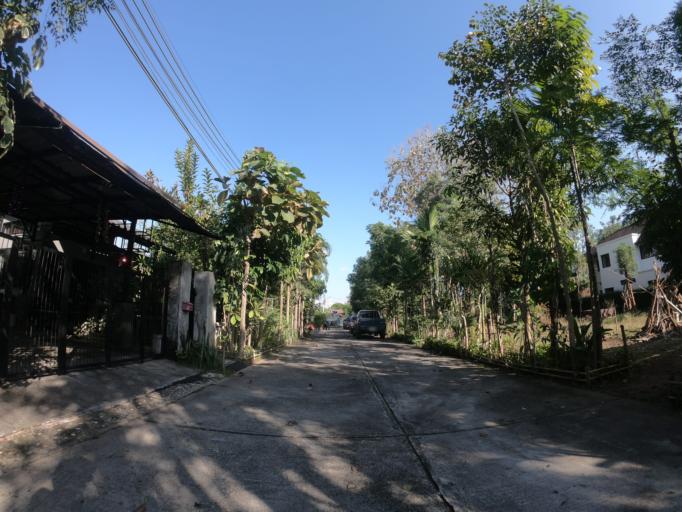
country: TH
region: Chiang Mai
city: Chiang Mai
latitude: 18.7535
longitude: 98.9716
